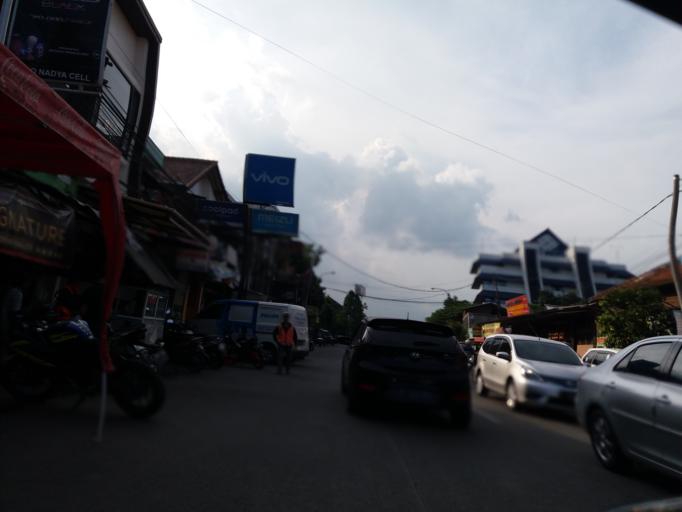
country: ID
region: West Java
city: Bandung
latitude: -6.9516
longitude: 107.6263
